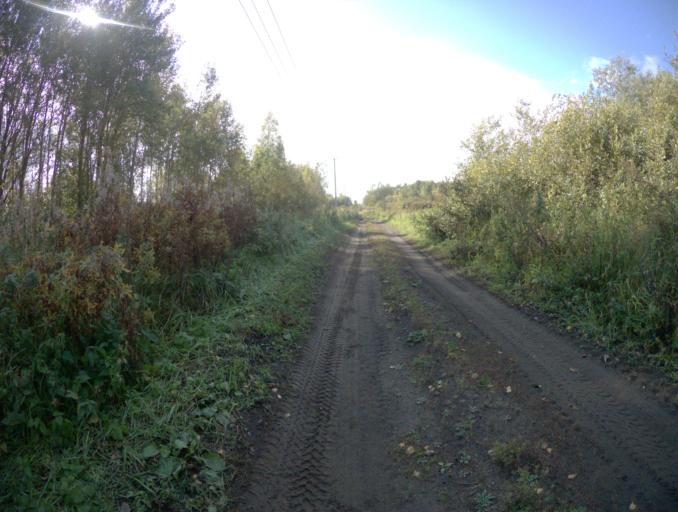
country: RU
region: Moskovskaya
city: Kerva
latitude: 55.7055
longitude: 39.5856
